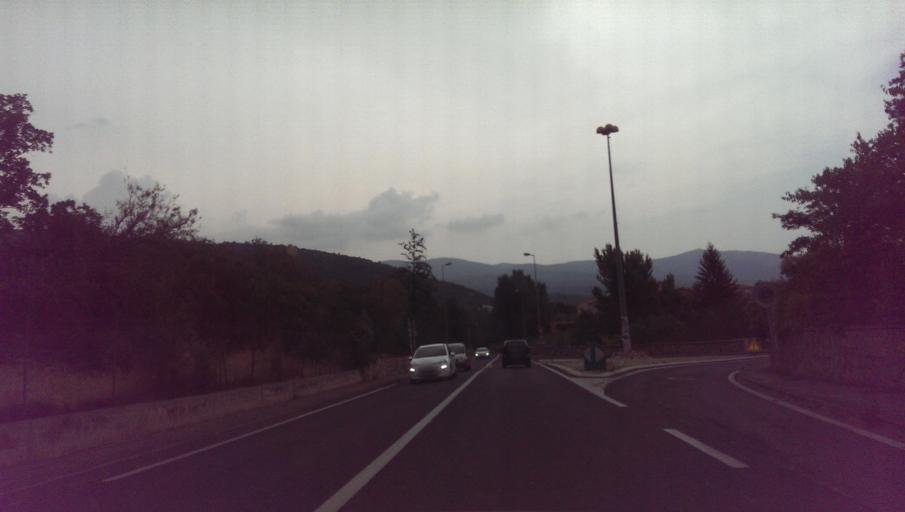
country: FR
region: Languedoc-Roussillon
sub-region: Departement des Pyrenees-Orientales
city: Ria-Sirach
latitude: 42.6139
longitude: 2.4113
